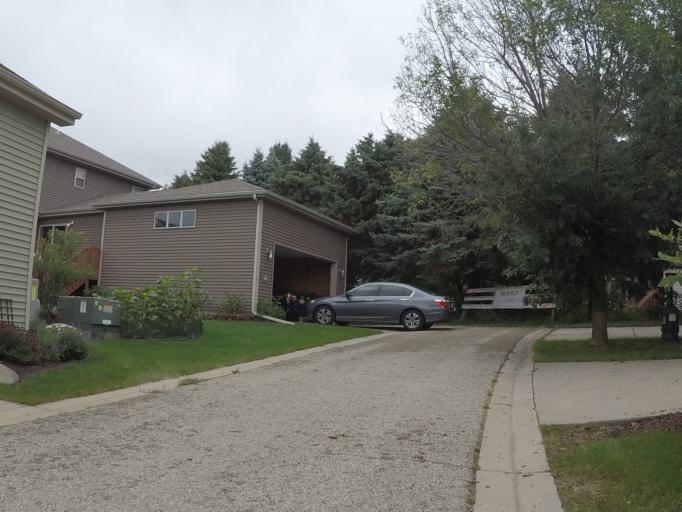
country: US
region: Wisconsin
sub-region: Dane County
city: Verona
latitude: 43.0446
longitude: -89.5422
